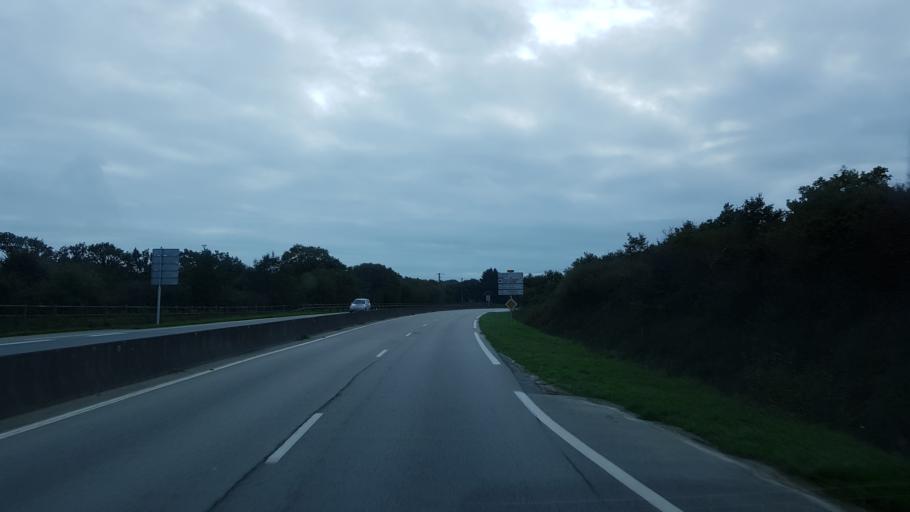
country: FR
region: Brittany
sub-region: Departement du Morbihan
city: Sarzeau
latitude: 47.5458
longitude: -2.7208
